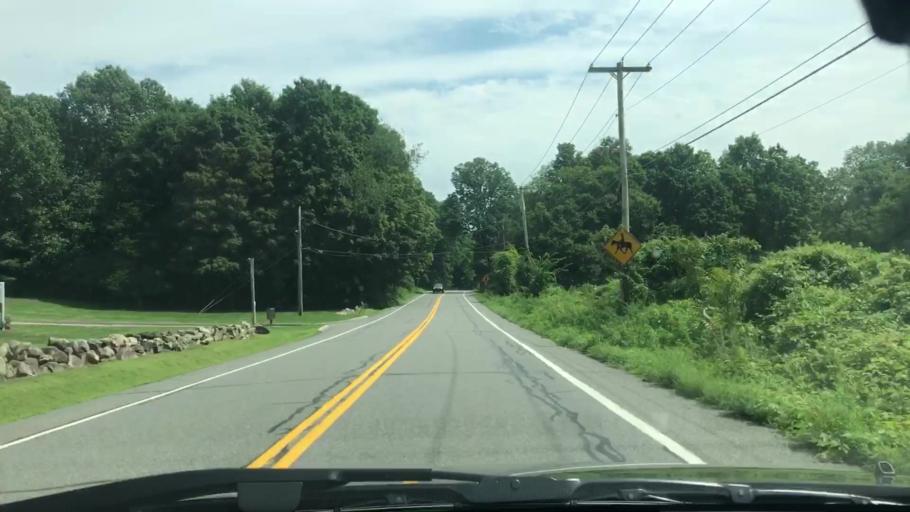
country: US
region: New York
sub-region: Westchester County
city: Bedford Hills
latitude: 41.2273
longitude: -73.6863
